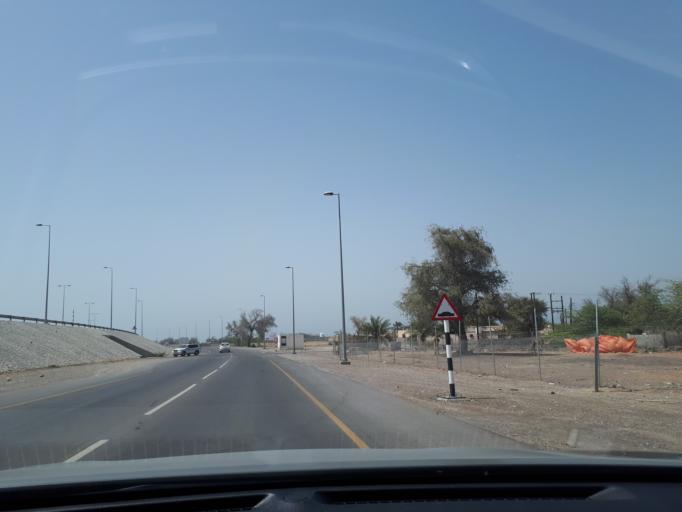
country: OM
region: Al Batinah
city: Barka'
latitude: 23.6930
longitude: 58.0228
